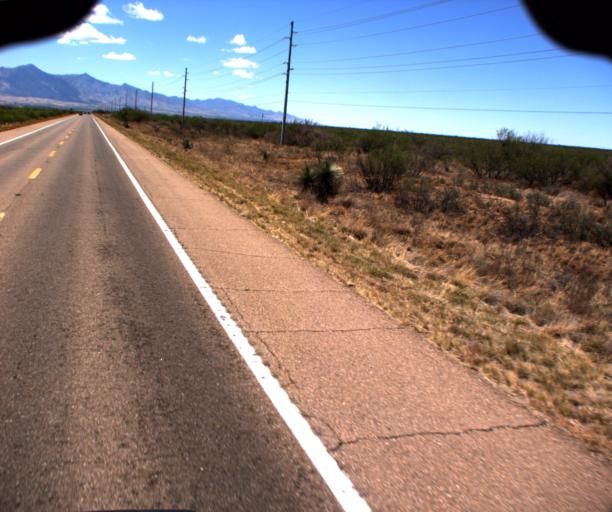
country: US
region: Arizona
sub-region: Cochise County
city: Naco
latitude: 31.3769
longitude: -110.0148
